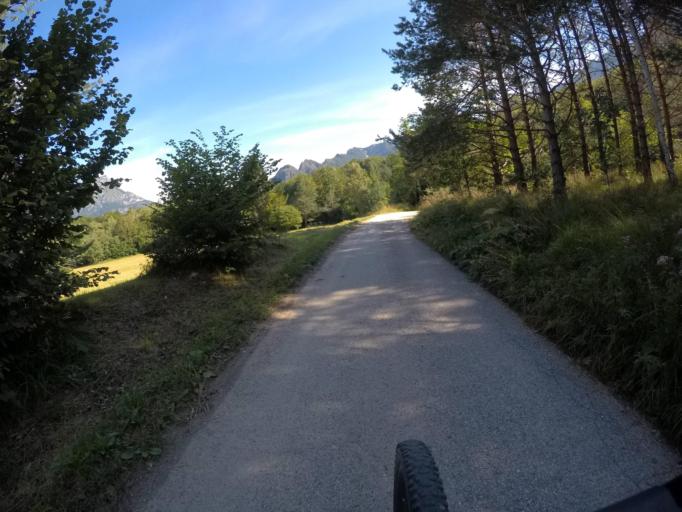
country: IT
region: Friuli Venezia Giulia
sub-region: Provincia di Udine
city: Zuglio
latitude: 46.4529
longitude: 13.0938
